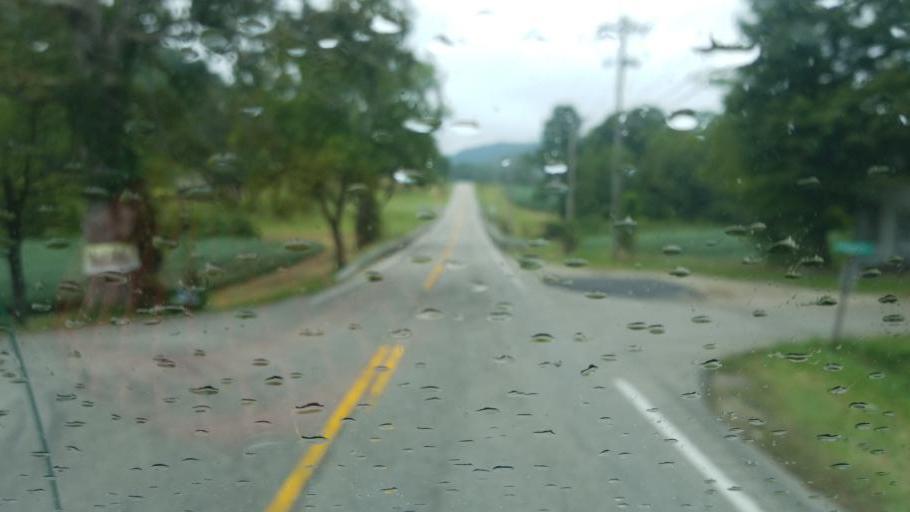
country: US
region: Kentucky
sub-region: Rowan County
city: Morehead
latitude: 38.2634
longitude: -83.4355
